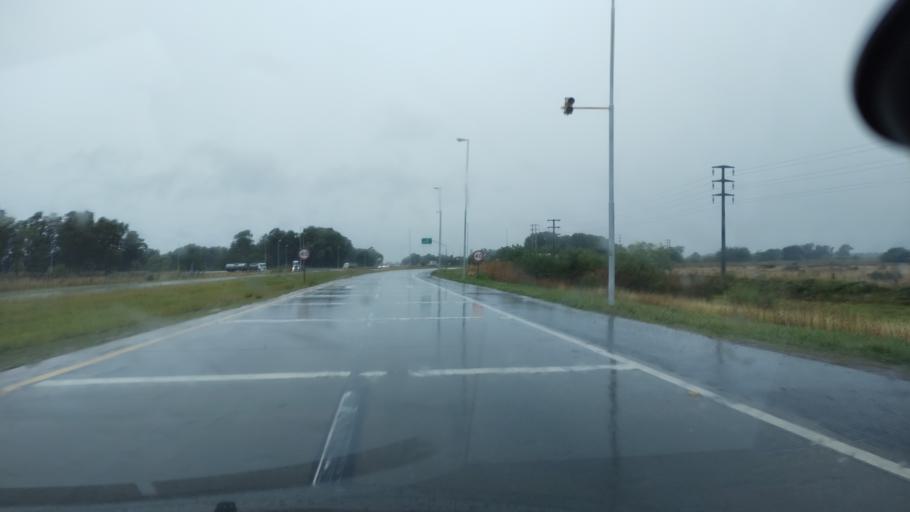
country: AR
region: Buenos Aires
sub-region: Partido de San Vicente
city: San Vicente
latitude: -35.0562
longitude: -58.4450
